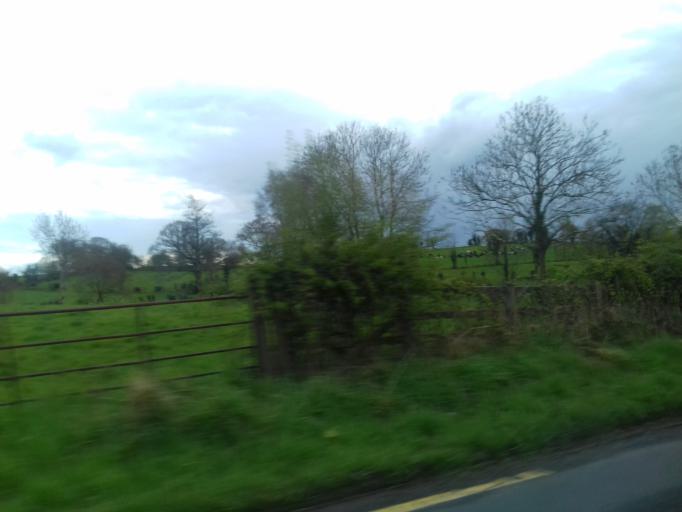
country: IE
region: Ulster
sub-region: An Cabhan
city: Ballyconnell
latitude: 54.0921
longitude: -7.5402
